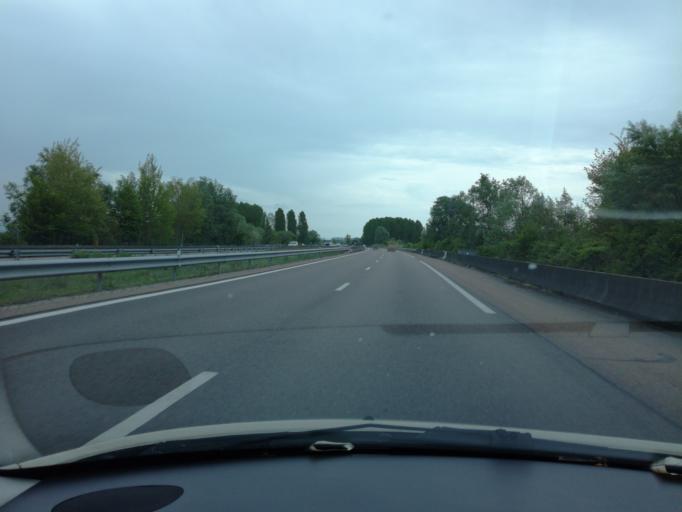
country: FR
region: Franche-Comte
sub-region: Departement du Jura
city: Mont-sous-Vaudrey
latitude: 46.9220
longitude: 5.5547
